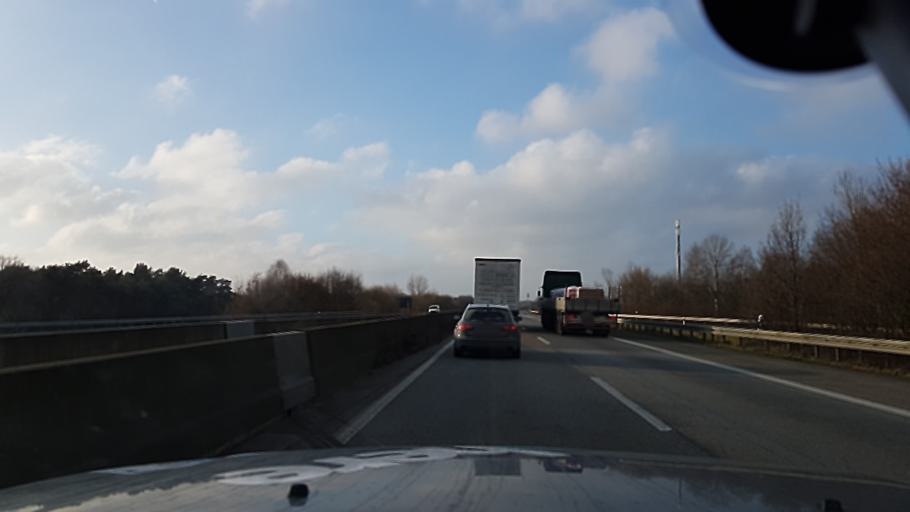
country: DE
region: North Rhine-Westphalia
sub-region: Regierungsbezirk Munster
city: Horstel
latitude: 52.2910
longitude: 7.5410
